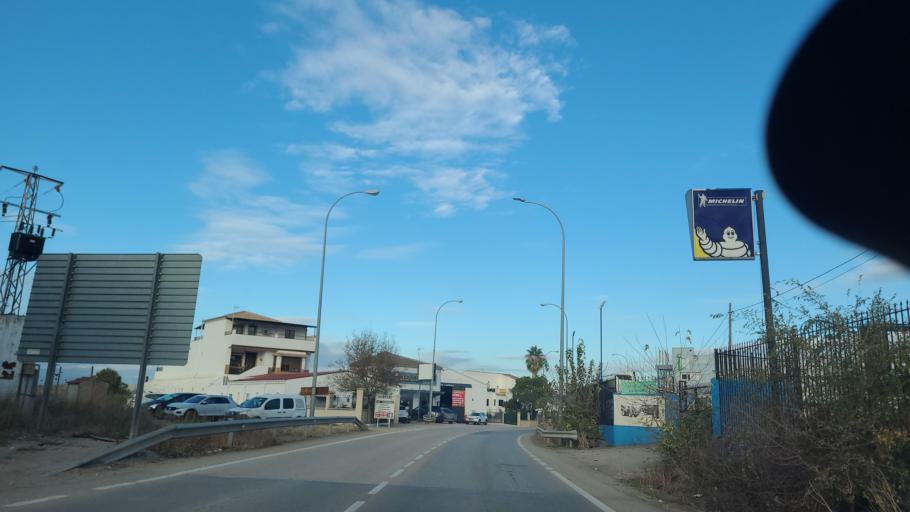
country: ES
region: Andalusia
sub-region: Provincia de Jaen
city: Mengibar
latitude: 37.9735
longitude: -3.7969
